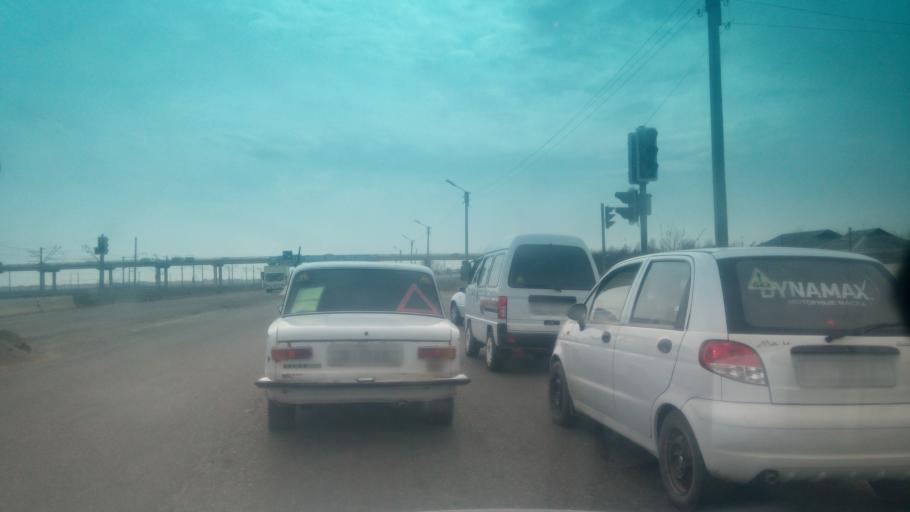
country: UZ
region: Sirdaryo
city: Guliston
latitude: 40.4736
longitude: 68.7703
